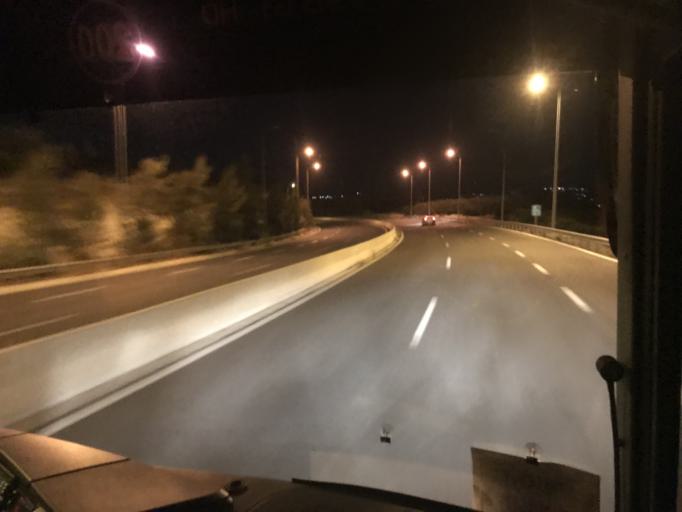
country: GR
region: Crete
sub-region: Nomos Irakleiou
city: Skalanion
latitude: 35.2652
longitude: 25.1839
